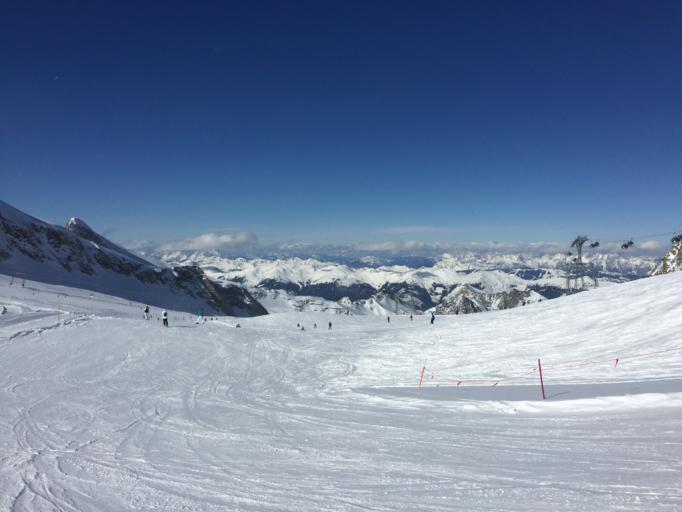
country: AT
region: Salzburg
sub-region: Politischer Bezirk Zell am See
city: Niedernsill
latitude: 47.1892
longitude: 12.6823
